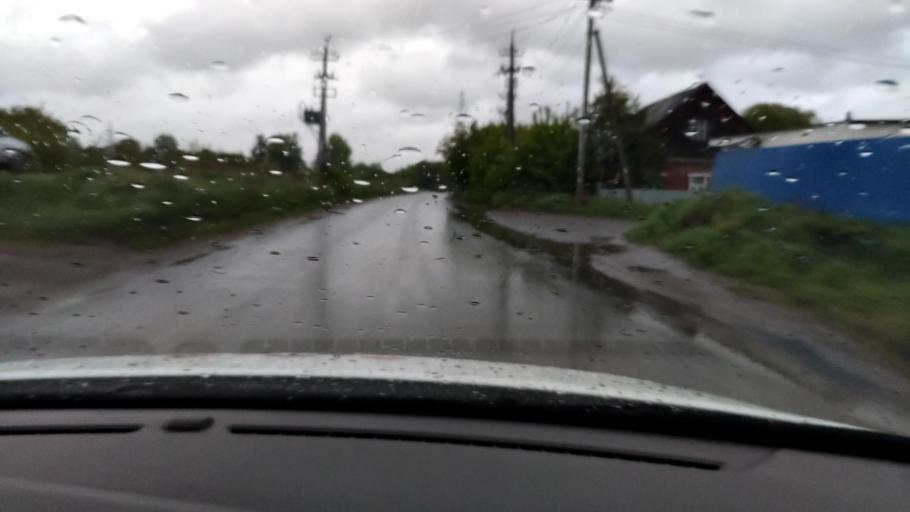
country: RU
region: Tatarstan
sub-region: Gorod Kazan'
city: Kazan
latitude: 55.7224
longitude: 49.1156
